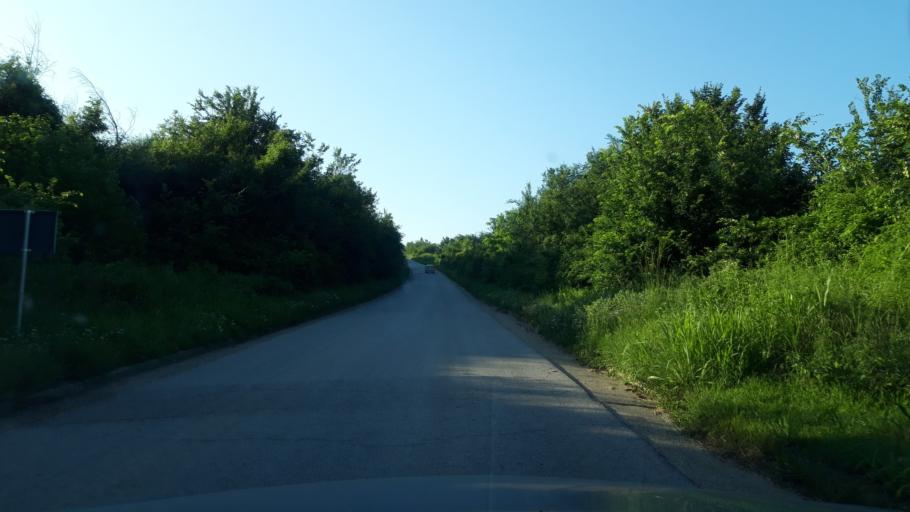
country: RS
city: Celarevo
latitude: 45.1247
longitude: 19.5084
